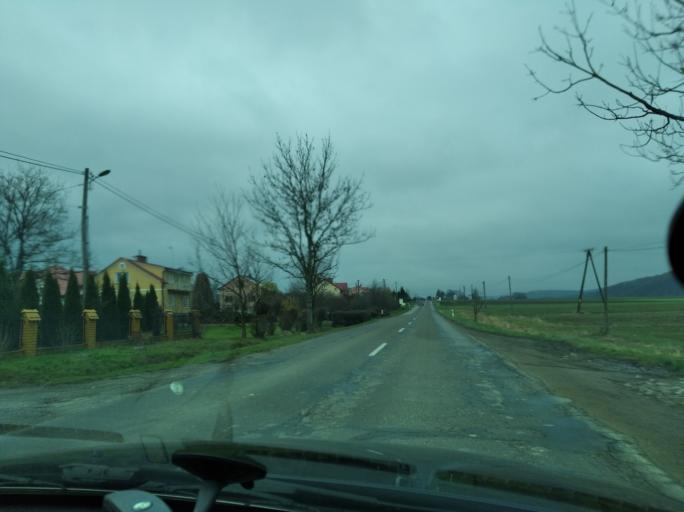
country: PL
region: Subcarpathian Voivodeship
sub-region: Powiat rzeszowski
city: Dynow
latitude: 49.8394
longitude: 22.2435
